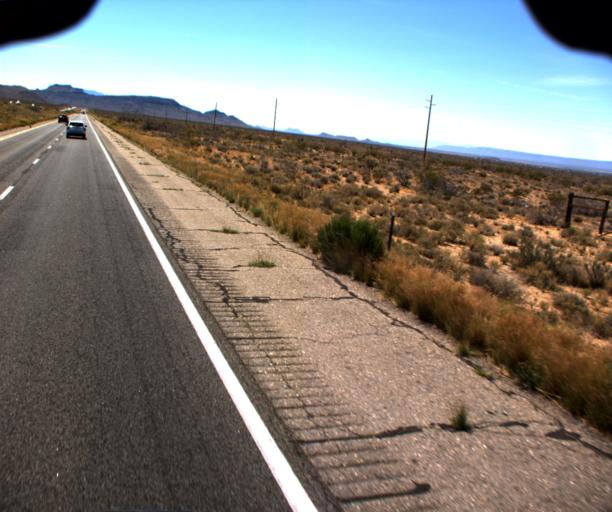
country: US
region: Arizona
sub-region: Mohave County
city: Golden Valley
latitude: 35.2726
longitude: -114.1696
